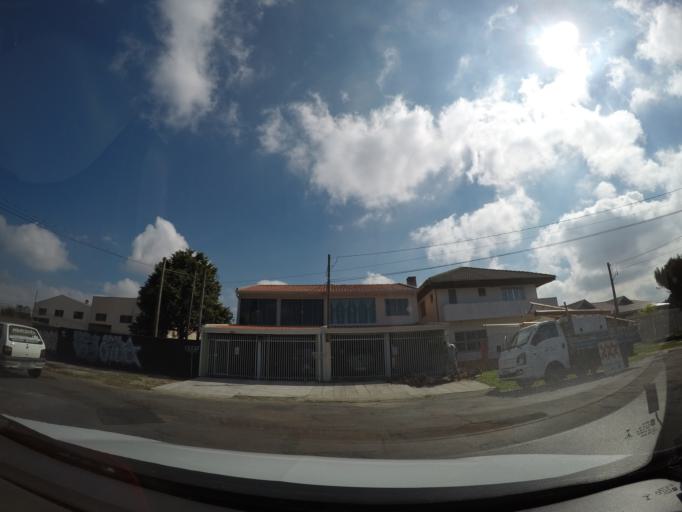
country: BR
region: Parana
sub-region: Sao Jose Dos Pinhais
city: Sao Jose dos Pinhais
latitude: -25.4972
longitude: -49.2190
